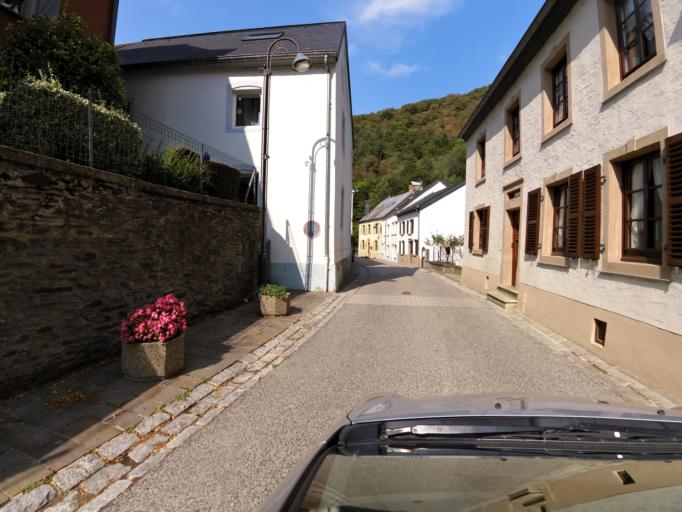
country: LU
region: Diekirch
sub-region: Canton de Wiltz
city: Esch-sur-Sure
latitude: 49.9123
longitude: 5.9354
